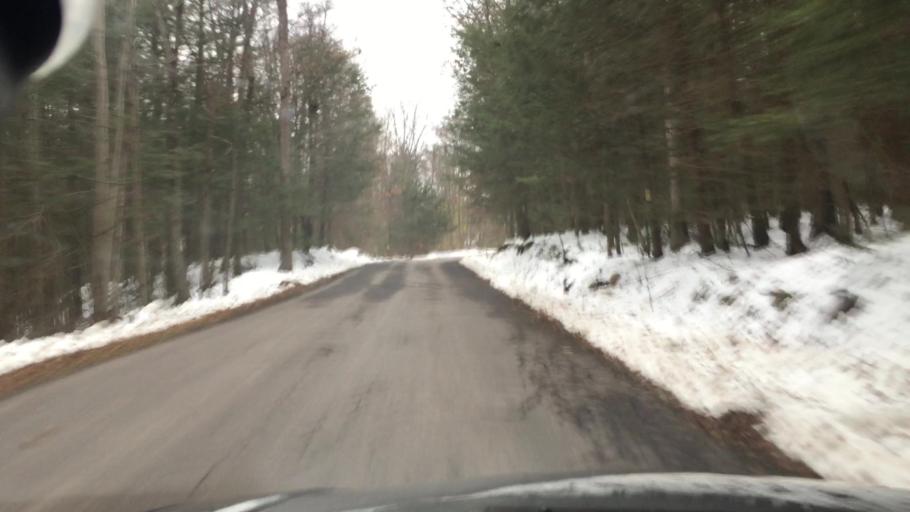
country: US
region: Pennsylvania
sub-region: Luzerne County
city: Conyngham
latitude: 41.0177
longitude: -76.0948
